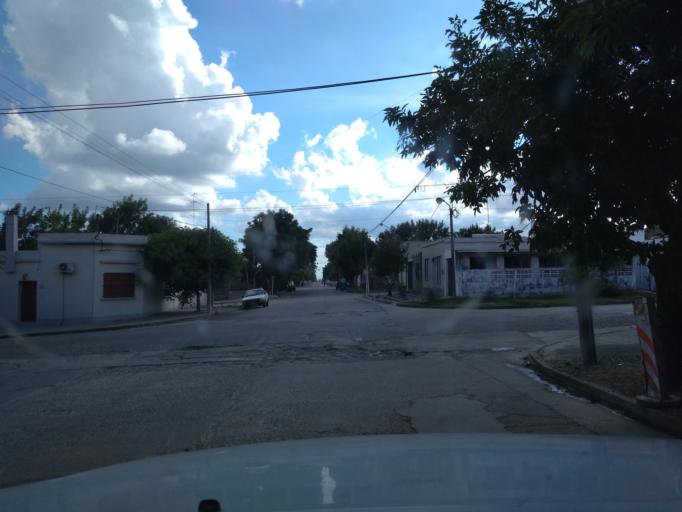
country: UY
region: Florida
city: Florida
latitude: -34.0905
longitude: -56.2171
